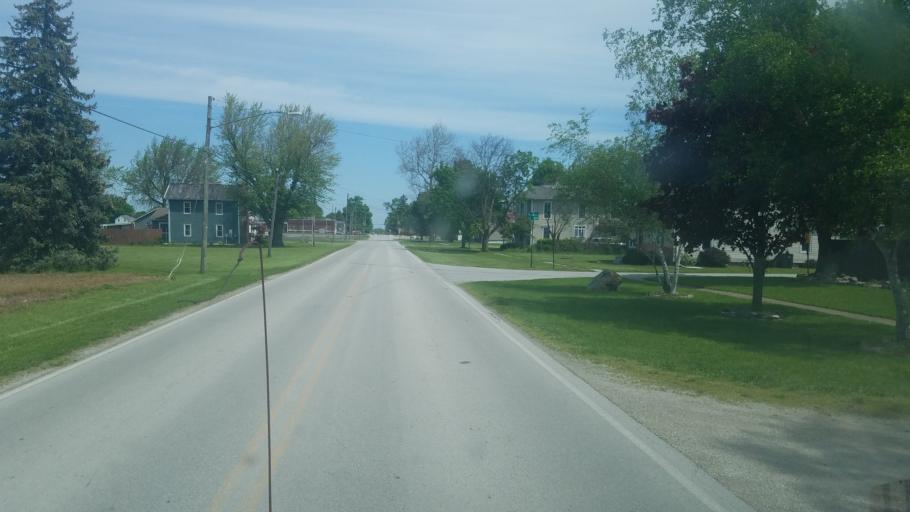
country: US
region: Ohio
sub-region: Sandusky County
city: Ballville
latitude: 41.2378
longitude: -83.1496
